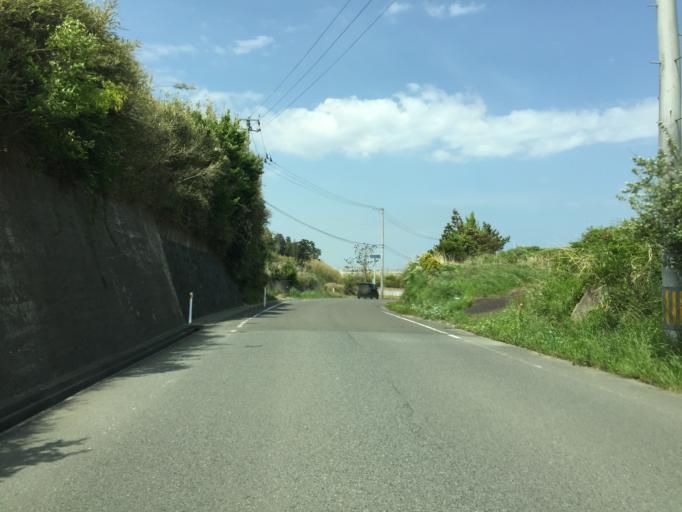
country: JP
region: Miyagi
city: Watari
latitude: 37.8956
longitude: 140.9294
